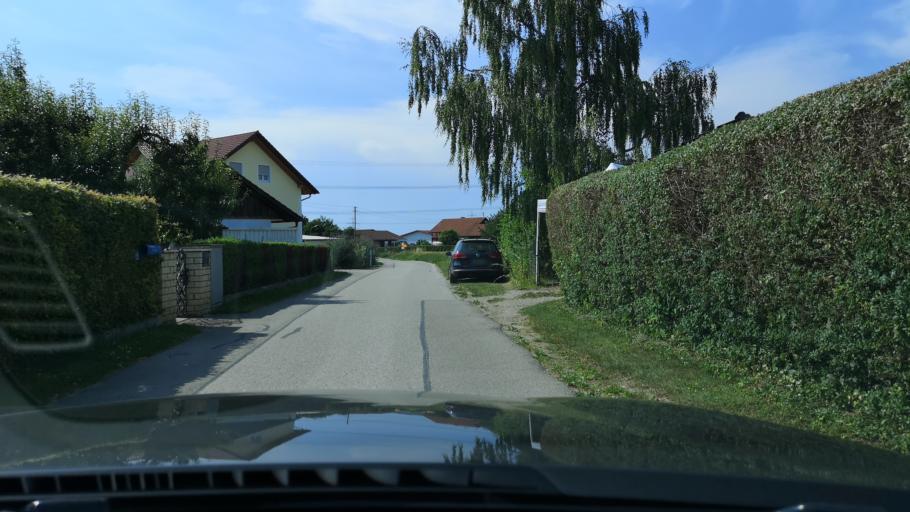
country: DE
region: Bavaria
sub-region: Upper Bavaria
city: Pliening
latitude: 48.1993
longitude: 11.7955
